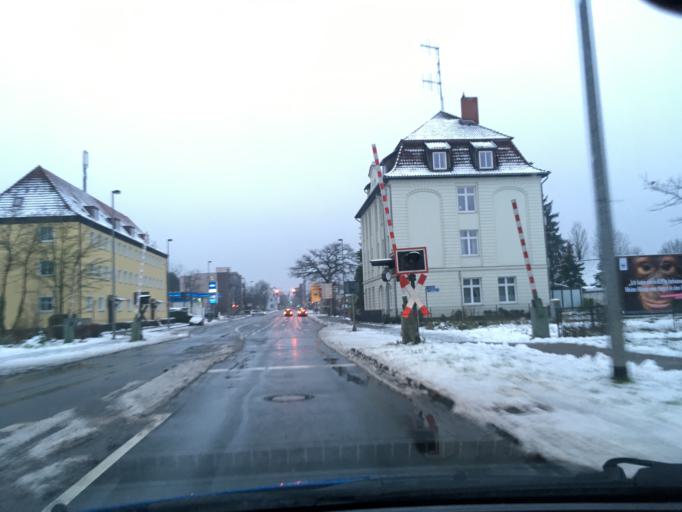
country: DE
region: Lower Saxony
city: Celle
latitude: 52.6356
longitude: 10.0801
